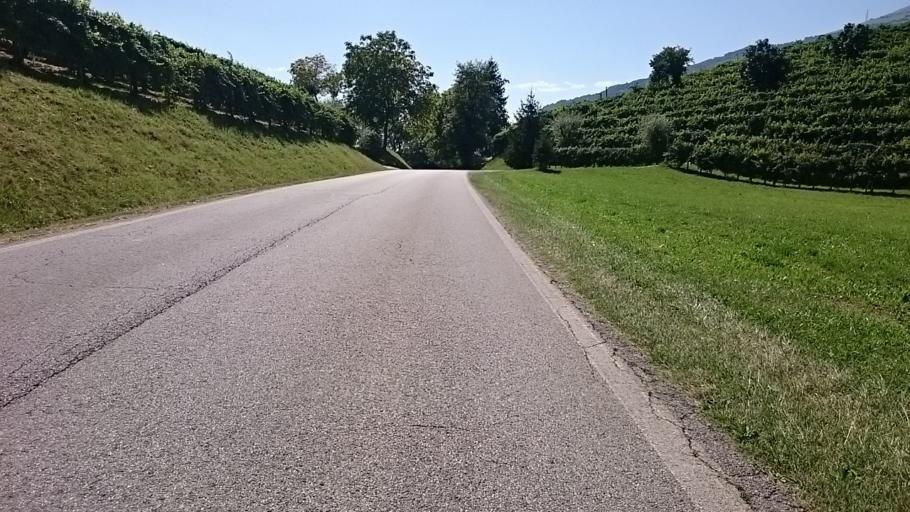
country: IT
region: Veneto
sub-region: Provincia di Treviso
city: Miane
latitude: 45.9196
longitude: 12.0859
